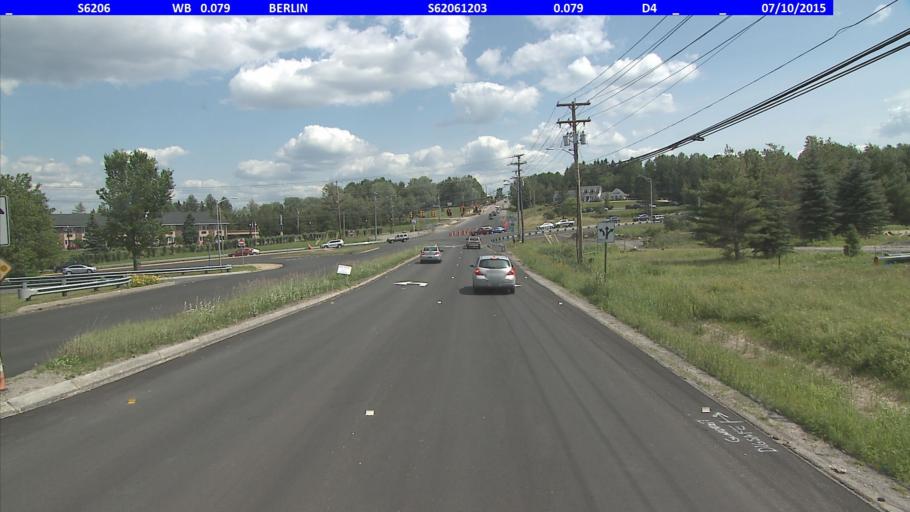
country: US
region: Vermont
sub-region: Washington County
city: Montpelier
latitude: 44.2191
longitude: -72.5608
